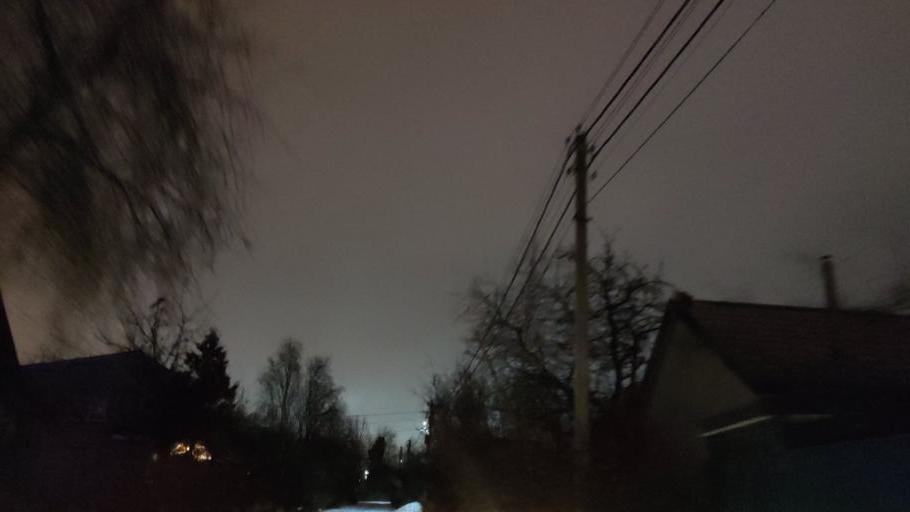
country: RU
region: Moscow
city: Vnukovo
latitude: 55.5976
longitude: 37.2368
